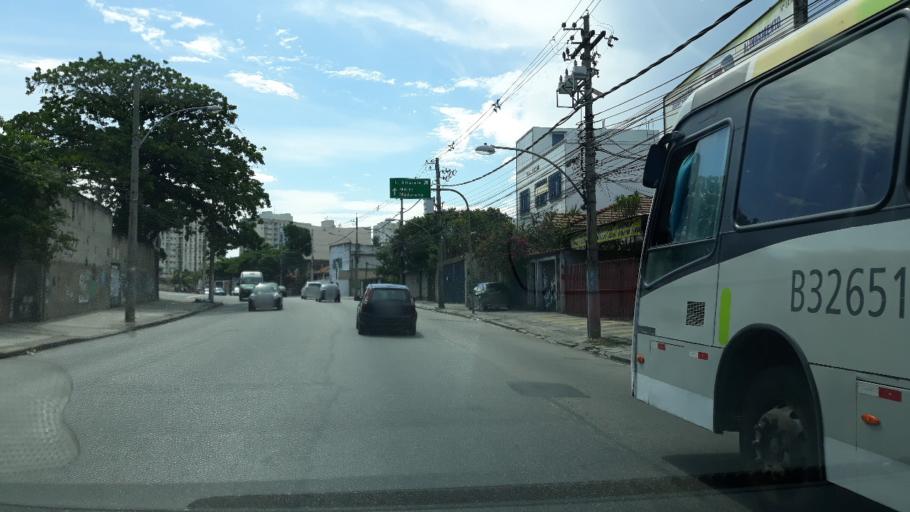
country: BR
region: Rio de Janeiro
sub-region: Rio De Janeiro
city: Rio de Janeiro
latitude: -22.8783
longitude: -43.2619
